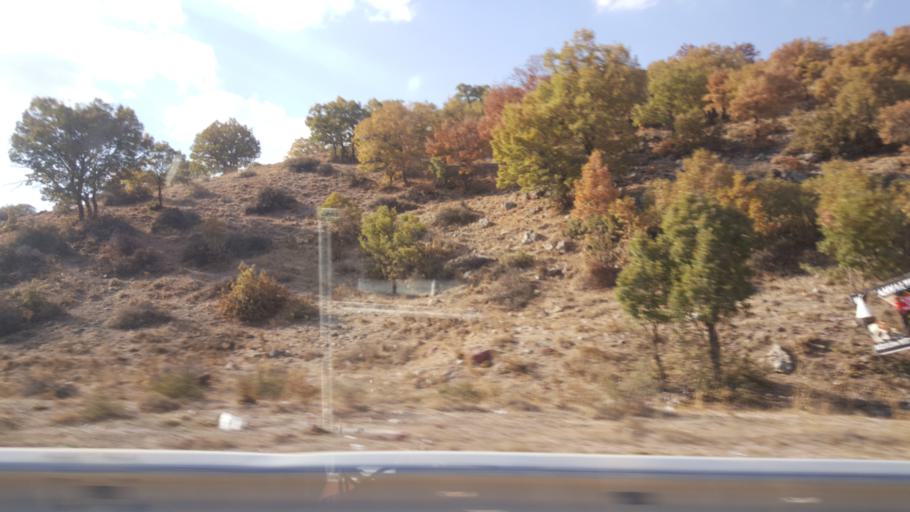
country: TR
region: Eskisehir
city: Kirka
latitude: 39.3333
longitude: 30.5775
